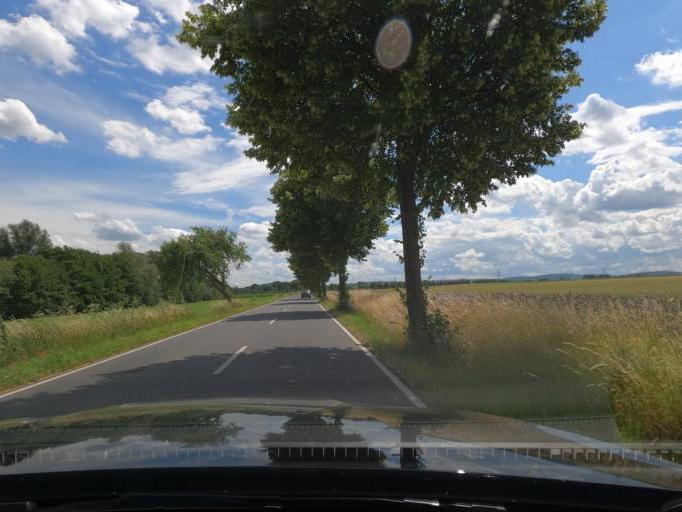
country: DE
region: Lower Saxony
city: Lengede
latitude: 52.1885
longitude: 10.3160
